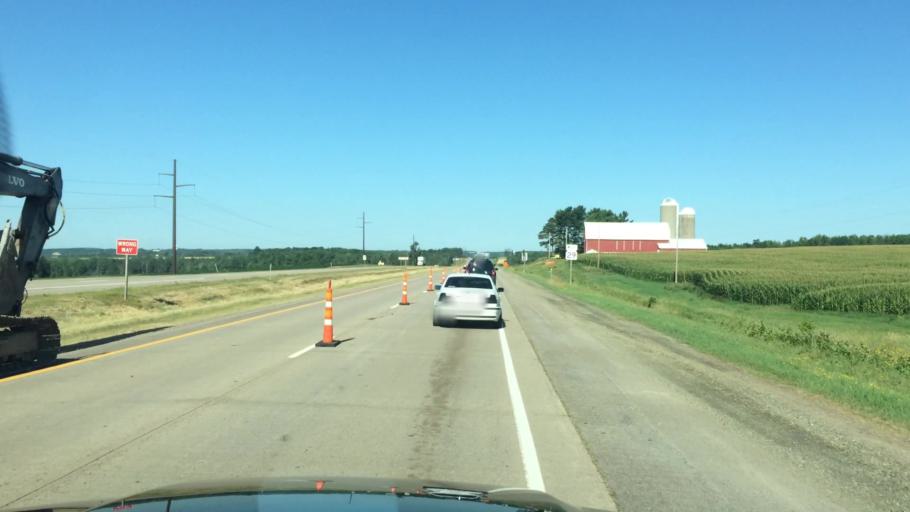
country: US
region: Wisconsin
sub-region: Marathon County
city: Edgar
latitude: 44.9446
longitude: -89.9061
